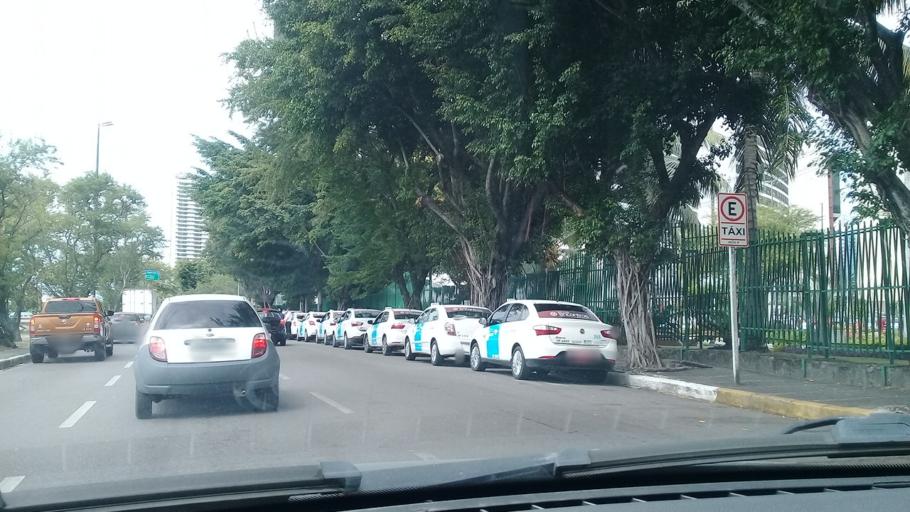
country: BR
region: Pernambuco
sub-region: Recife
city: Recife
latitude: -8.1176
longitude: -34.9055
